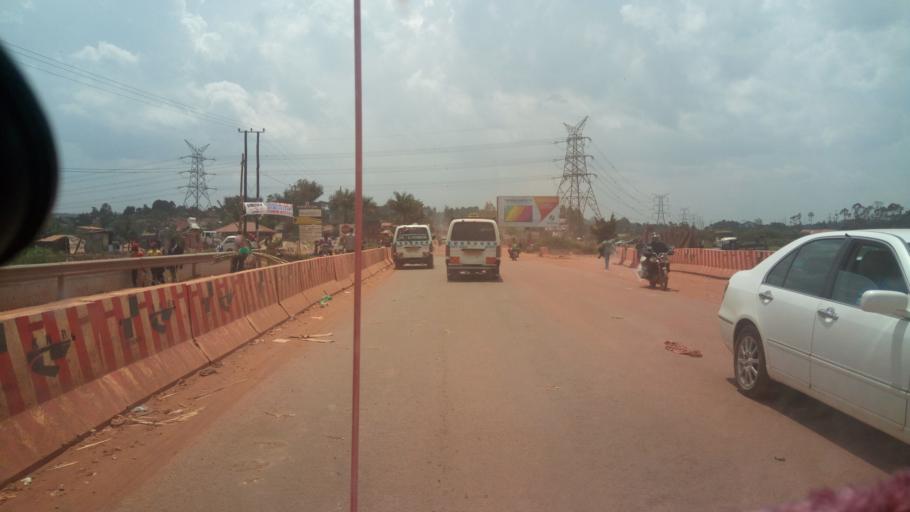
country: UG
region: Central Region
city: Kampala Central Division
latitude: 0.3466
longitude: 32.5415
